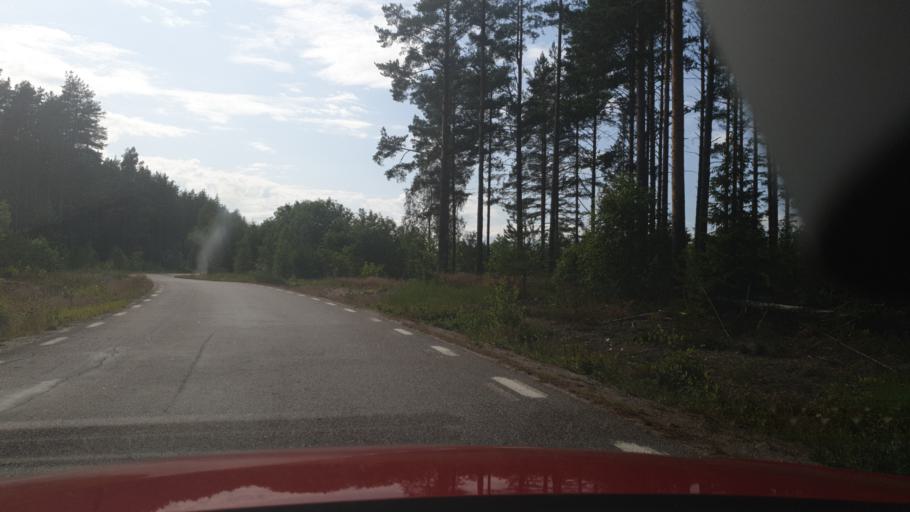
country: SE
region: Vaesternorrland
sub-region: Sundsvalls Kommun
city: Njurundabommen
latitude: 62.0366
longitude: 17.3633
